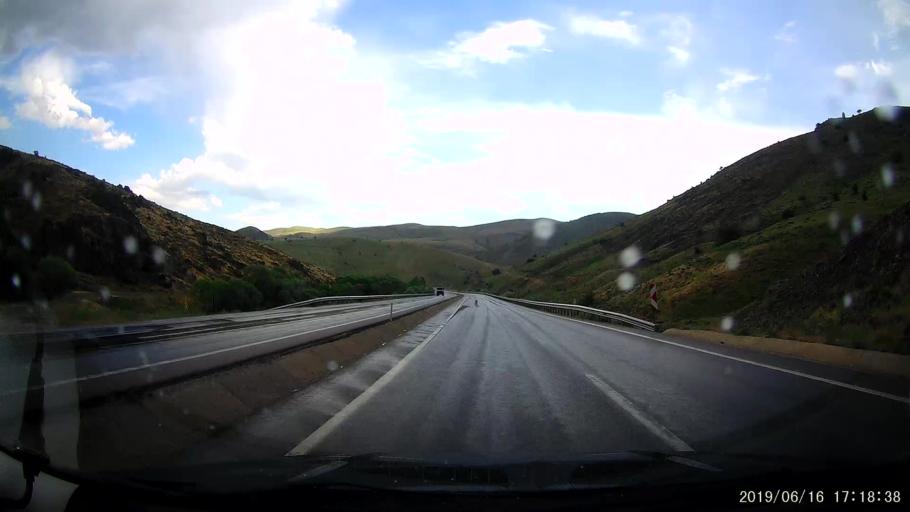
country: TR
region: Erzincan
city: Tercan
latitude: 39.8112
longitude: 40.5290
